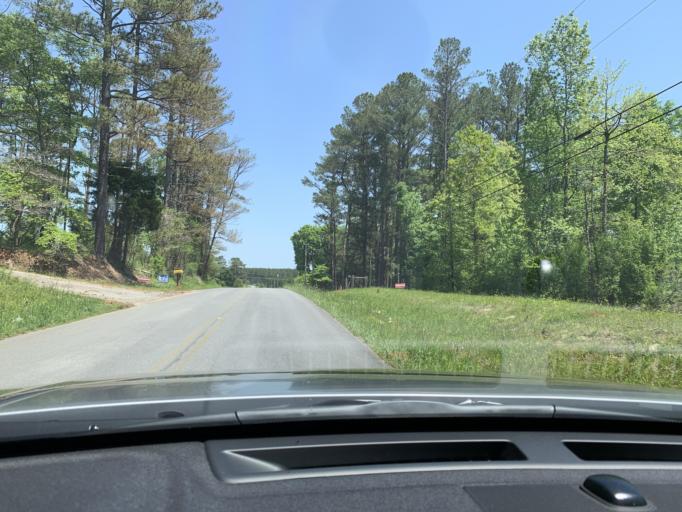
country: US
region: Georgia
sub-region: Polk County
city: Cedartown
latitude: 34.0444
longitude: -85.1877
